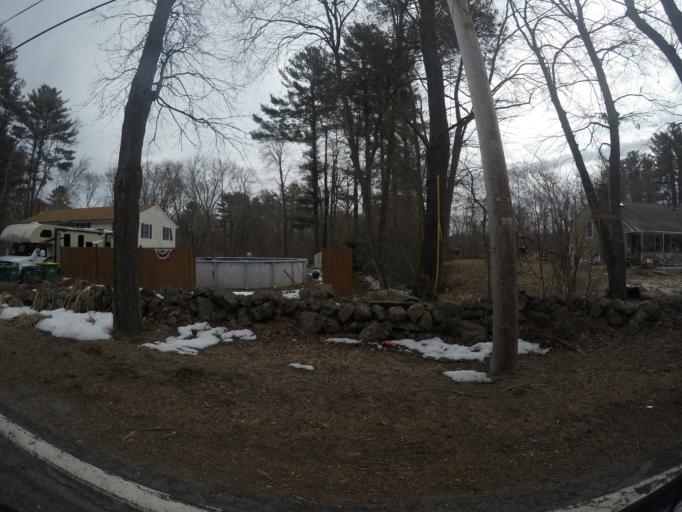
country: US
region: Massachusetts
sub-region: Bristol County
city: Easton
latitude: 42.0262
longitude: -71.1197
